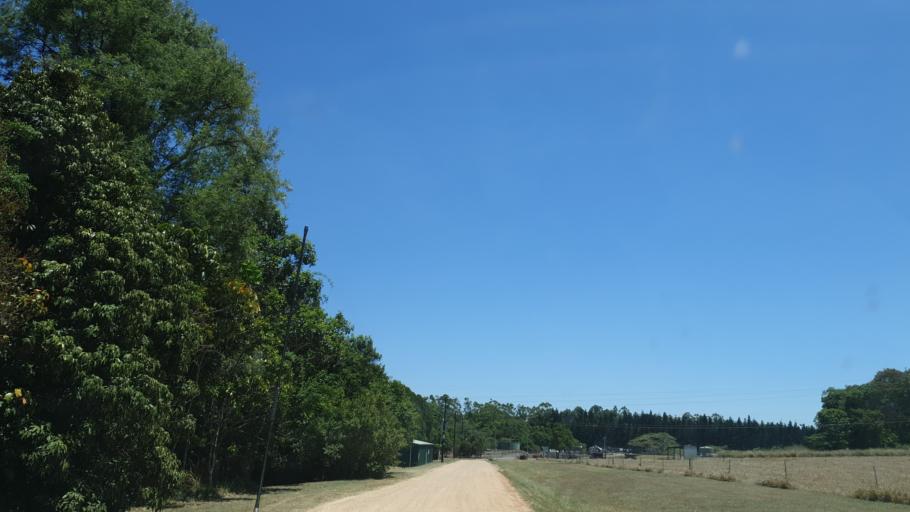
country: AU
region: Queensland
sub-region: Tablelands
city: Atherton
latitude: -17.2568
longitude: 145.4799
